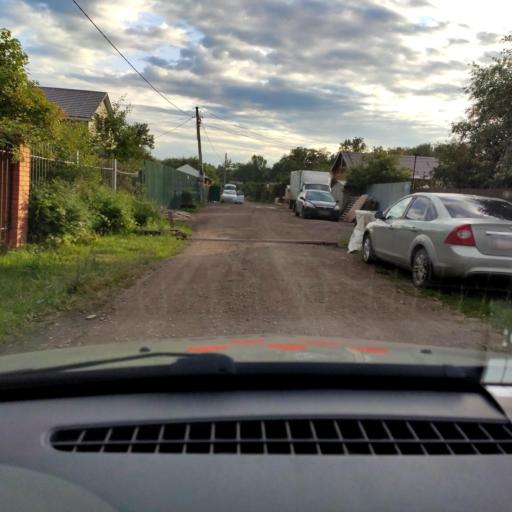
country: RU
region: Bashkortostan
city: Ufa
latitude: 54.6876
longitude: 55.8819
